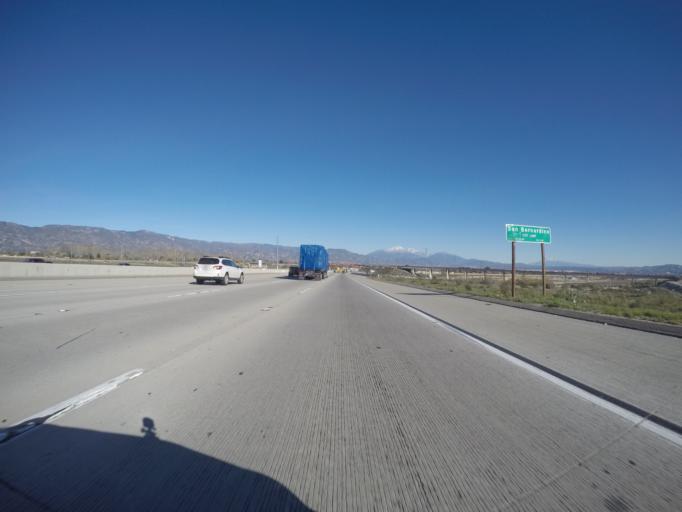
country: US
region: California
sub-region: San Bernardino County
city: Muscoy
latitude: 34.1343
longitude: -117.3495
